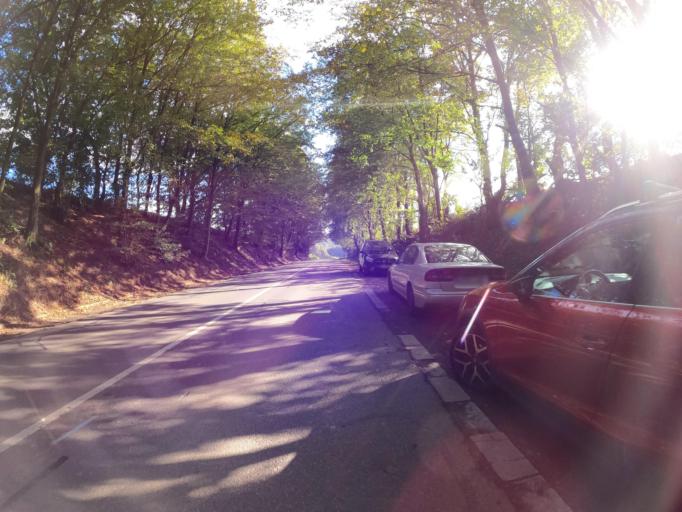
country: DE
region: North Rhine-Westphalia
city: Radevormwald
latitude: 51.2193
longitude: 7.3499
